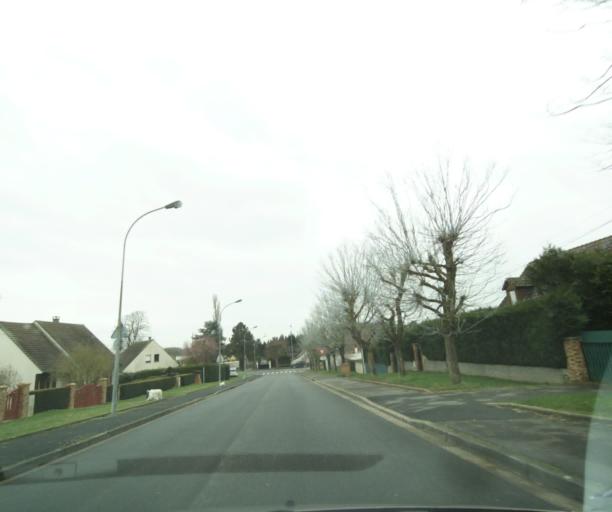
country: FR
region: Picardie
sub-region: Departement de l'Oise
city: Noyon
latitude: 49.5795
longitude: 3.0194
